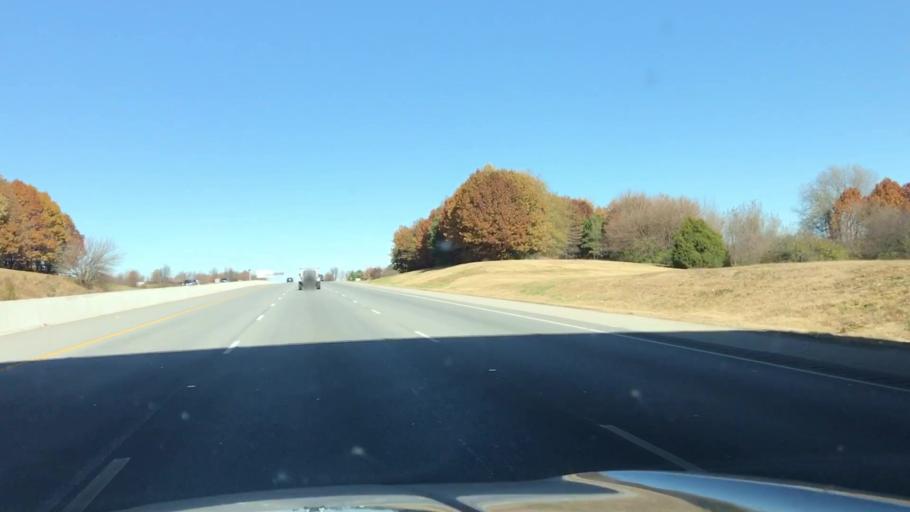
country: US
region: Arkansas
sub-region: Benton County
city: Lowell
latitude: 36.2543
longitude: -94.1503
